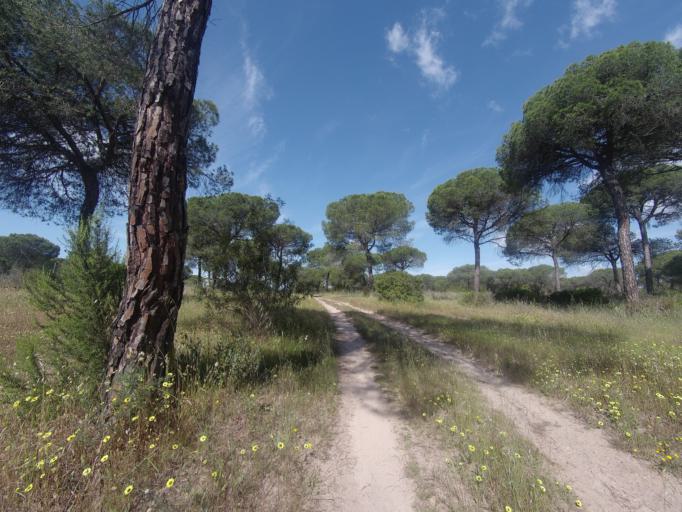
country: ES
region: Andalusia
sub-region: Provincia de Huelva
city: Aljaraque
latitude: 37.2342
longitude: -7.0646
